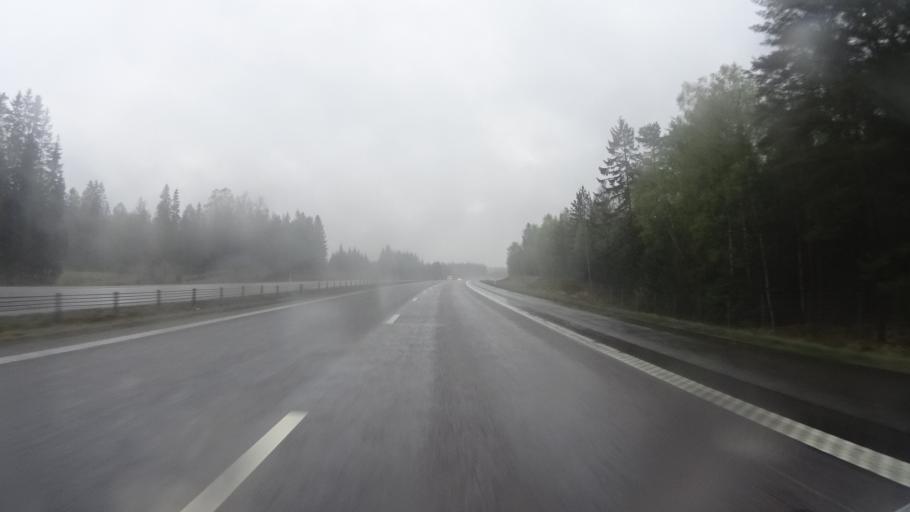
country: SE
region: Kronoberg
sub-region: Markaryds Kommun
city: Stromsnasbruk
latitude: 56.5822
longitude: 13.7221
